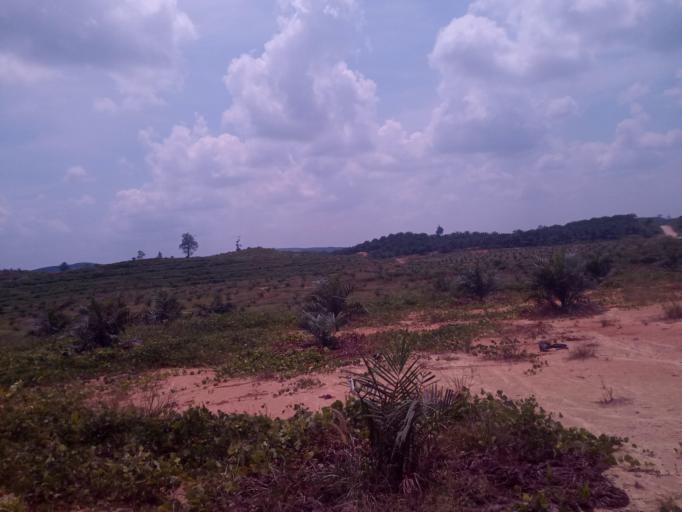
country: ID
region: Jambi
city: Sungaibengkal
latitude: -1.4966
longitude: 102.9099
